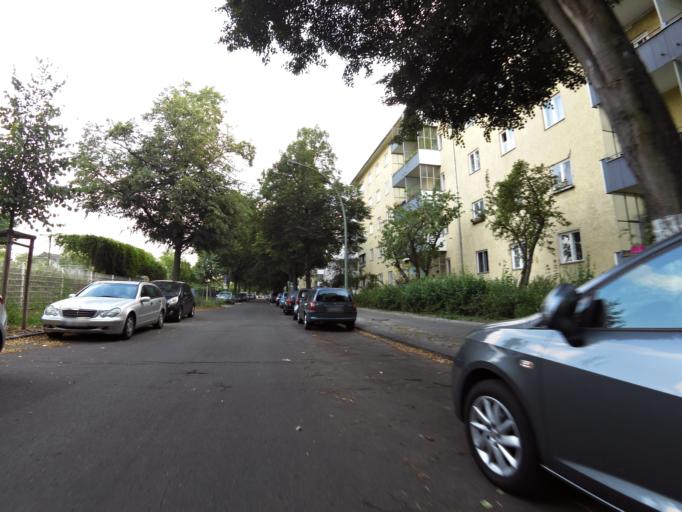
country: DE
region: Berlin
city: Schoneberg Bezirk
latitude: 52.4647
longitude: 13.3497
